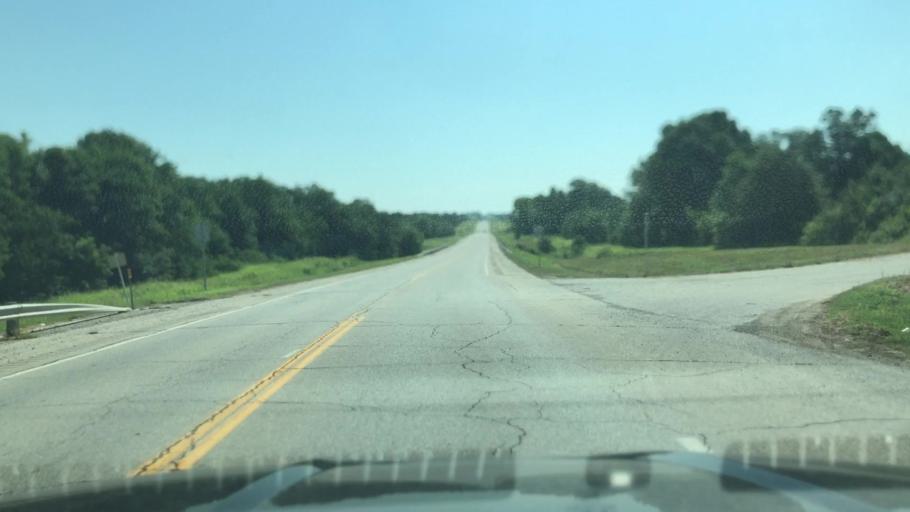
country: US
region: Oklahoma
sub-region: Creek County
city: Drumright
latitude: 35.9885
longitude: -96.5732
